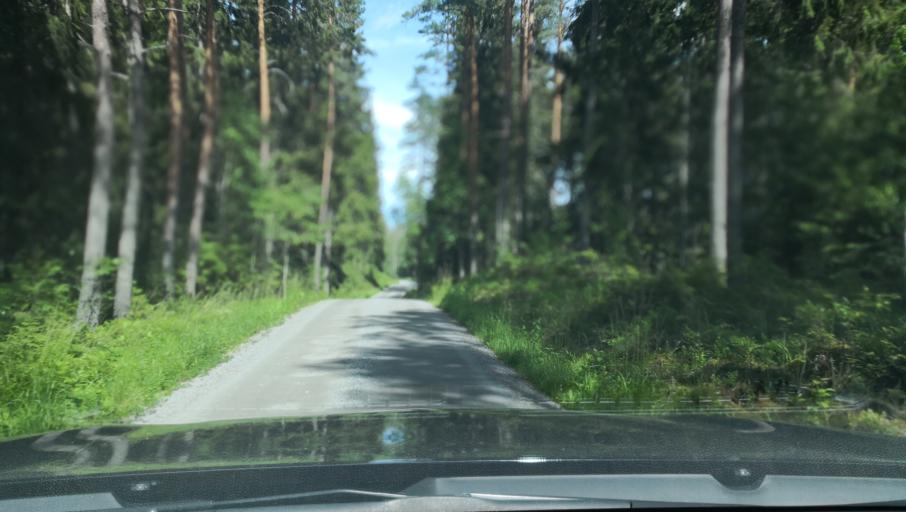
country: SE
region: Vaestmanland
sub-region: Surahammars Kommun
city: Ramnas
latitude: 59.8852
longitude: 16.0937
